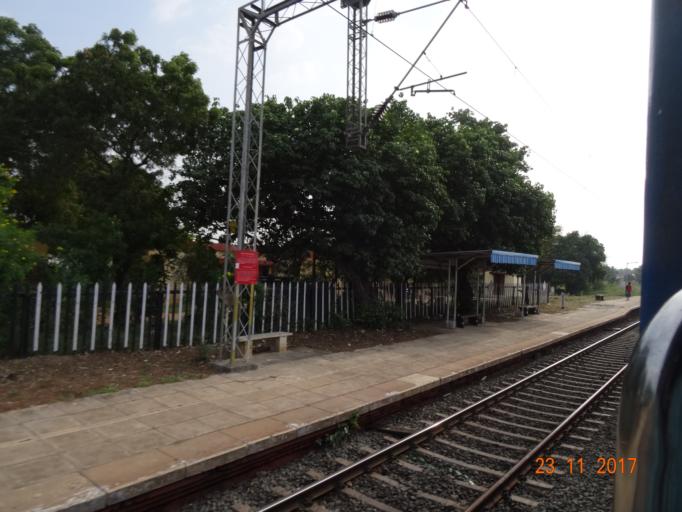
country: IN
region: Tamil Nadu
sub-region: Coimbatore
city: Sulur
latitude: 11.0490
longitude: 77.1165
